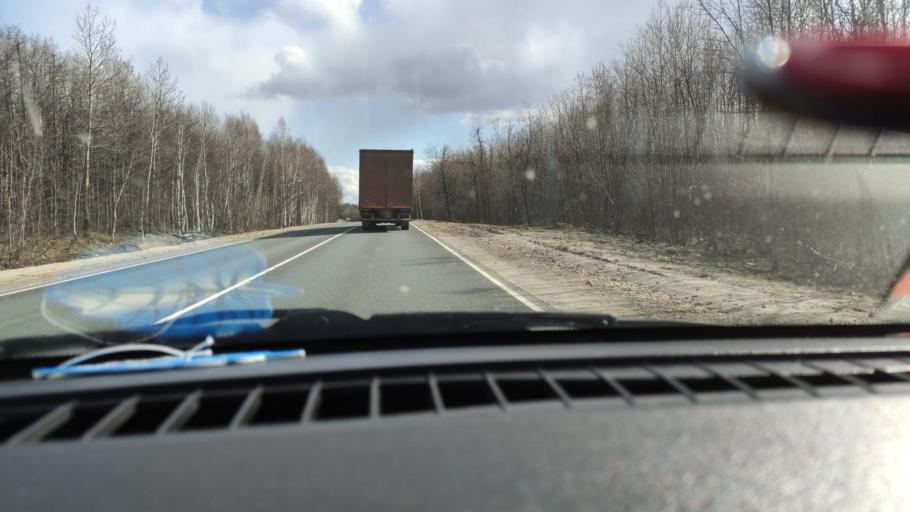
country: RU
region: Saratov
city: Khvalynsk
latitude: 52.4716
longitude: 48.0153
